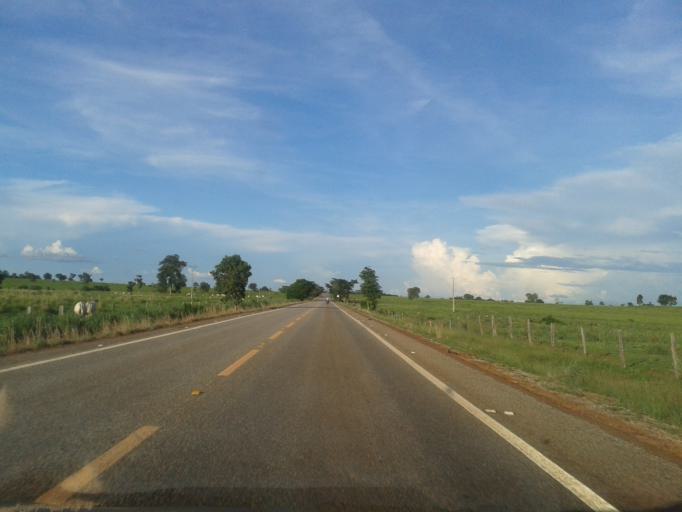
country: BR
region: Goias
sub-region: Sao Miguel Do Araguaia
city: Sao Miguel do Araguaia
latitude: -13.4227
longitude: -50.2750
